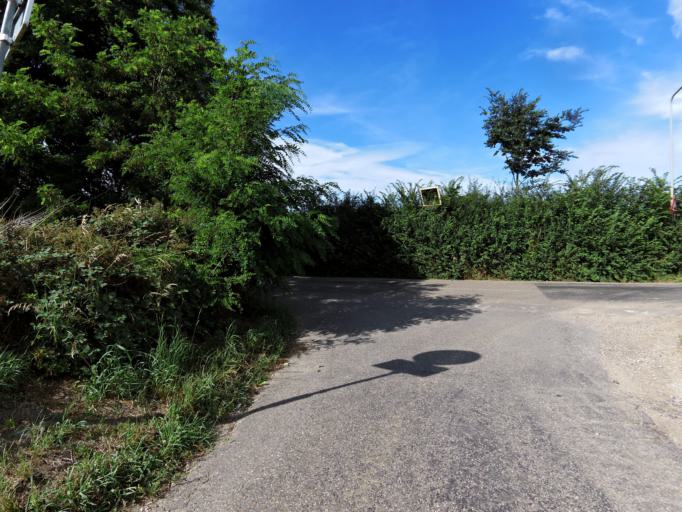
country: NL
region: Limburg
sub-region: Gemeente Onderbanken
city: Merkelbeek
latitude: 50.9808
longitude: 5.9473
